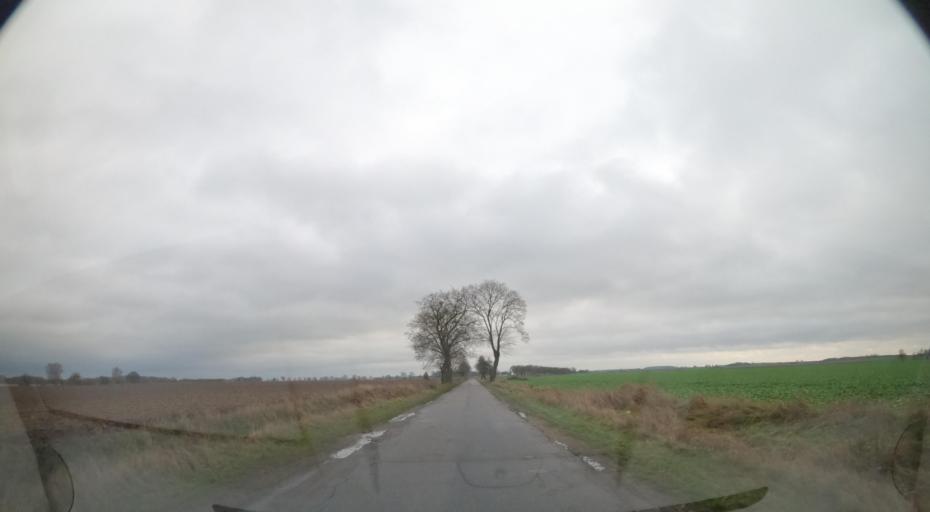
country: PL
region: Greater Poland Voivodeship
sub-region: Powiat zlotowski
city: Zlotow
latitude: 53.2789
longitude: 17.0907
